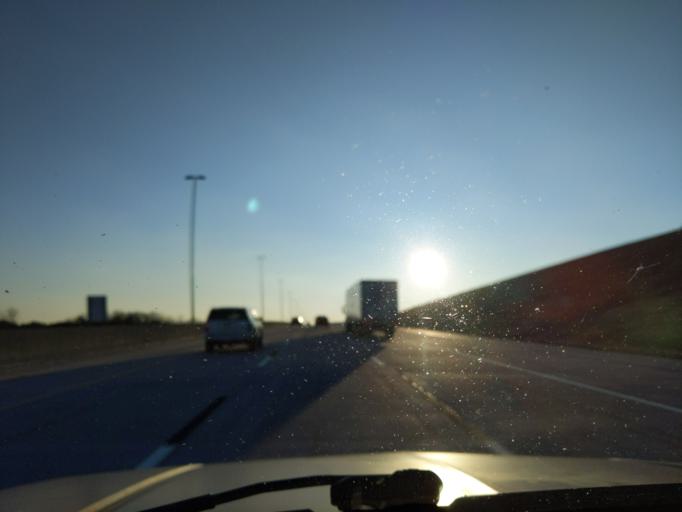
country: US
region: Oklahoma
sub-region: Creek County
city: Kellyville
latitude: 35.9756
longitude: -96.2106
